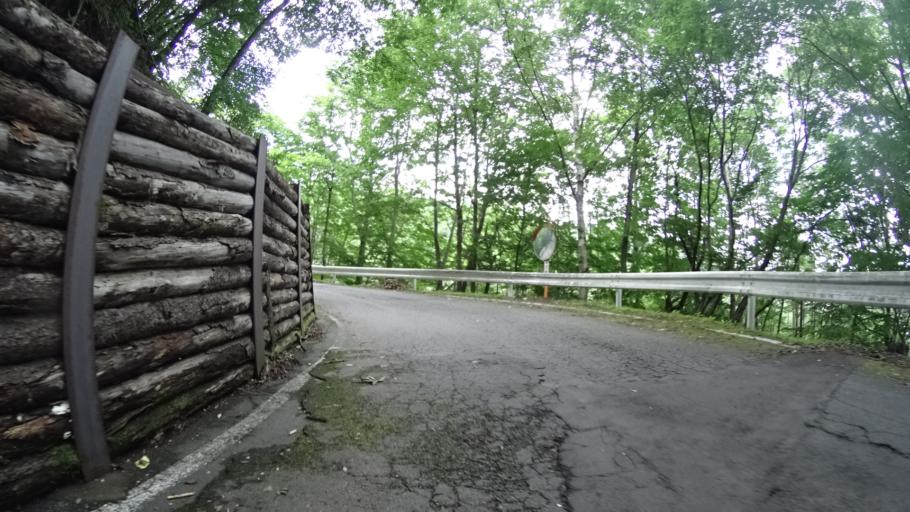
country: JP
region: Nagano
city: Saku
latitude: 36.0685
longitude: 138.6497
